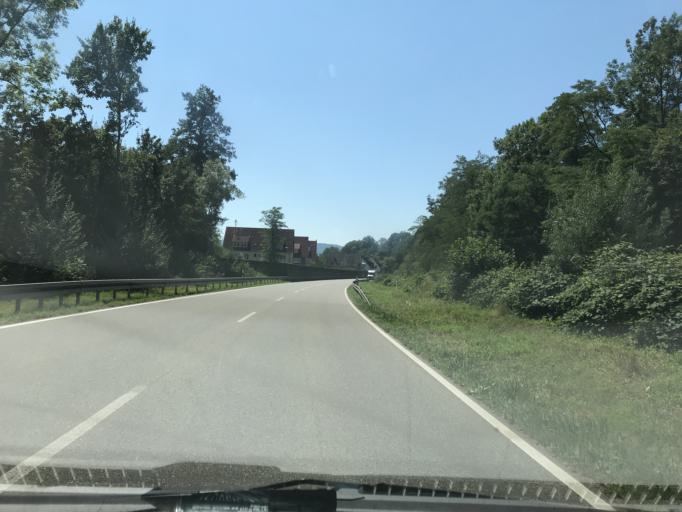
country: DE
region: Baden-Wuerttemberg
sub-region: Freiburg Region
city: Wehr
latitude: 47.5997
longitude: 7.9132
